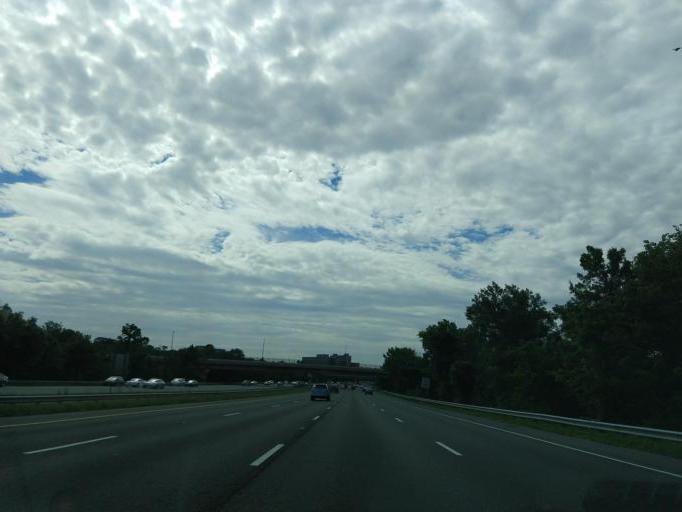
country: US
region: Maryland
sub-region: Prince George's County
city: Berwyn Heights
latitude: 39.0131
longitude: -76.9061
